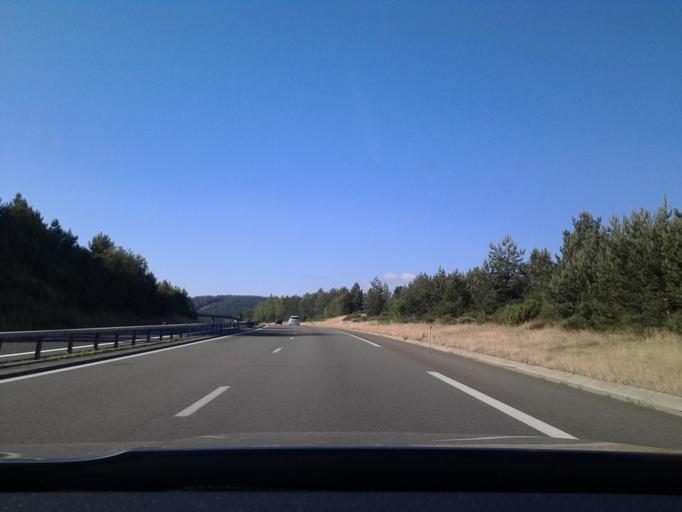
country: FR
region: Languedoc-Roussillon
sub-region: Departement de la Lozere
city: Aumont-Aubrac
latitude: 44.6773
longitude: 3.2594
